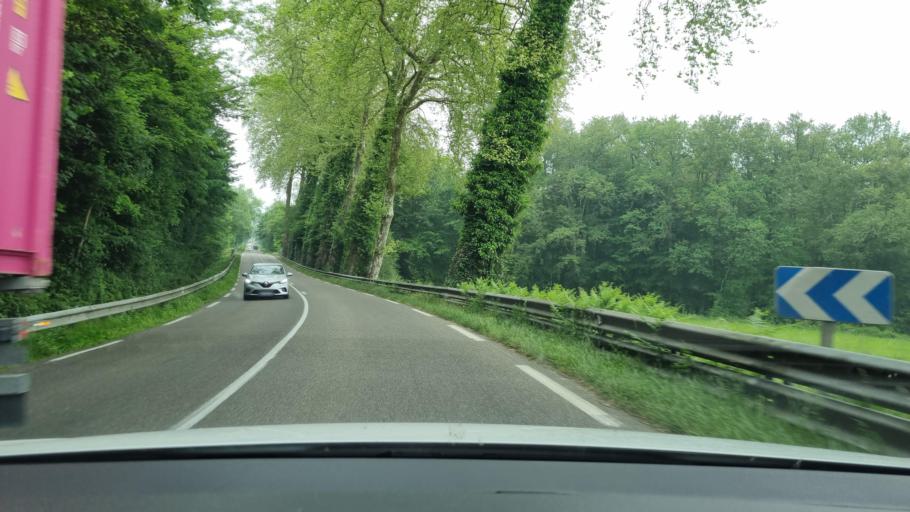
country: FR
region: Aquitaine
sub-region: Departement des Landes
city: Saint-Sever
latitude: 43.7314
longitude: -0.5716
